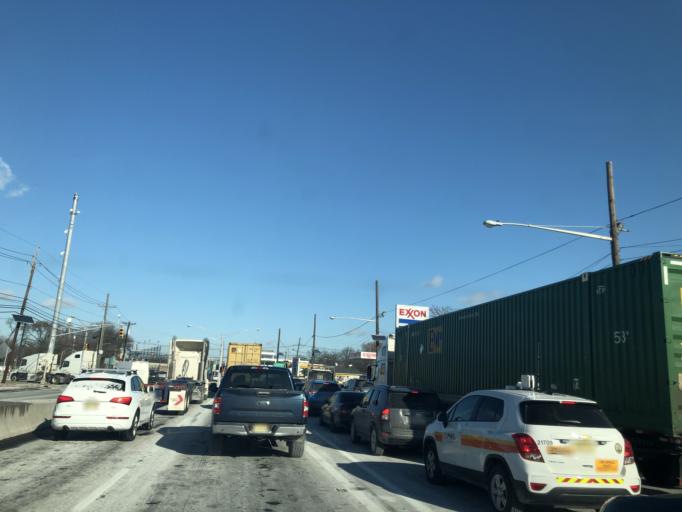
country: US
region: New Jersey
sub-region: Hudson County
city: Jersey City
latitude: 40.7230
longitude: -74.0910
